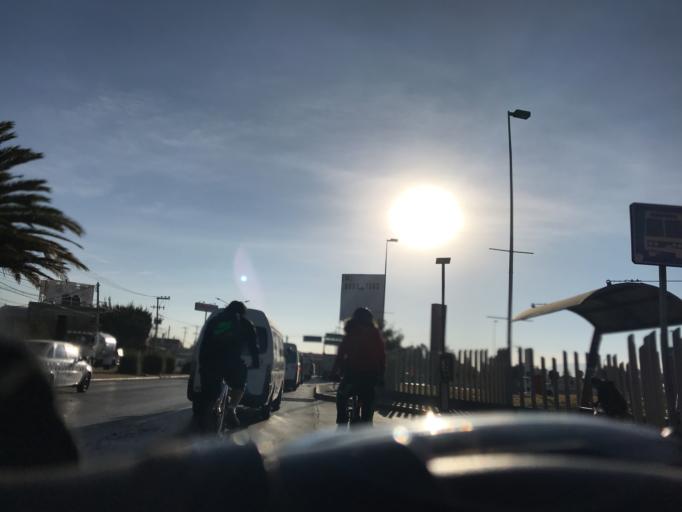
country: MX
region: Mexico
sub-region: Cuautitlan
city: La Trinidad
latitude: 19.6730
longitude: -99.1662
